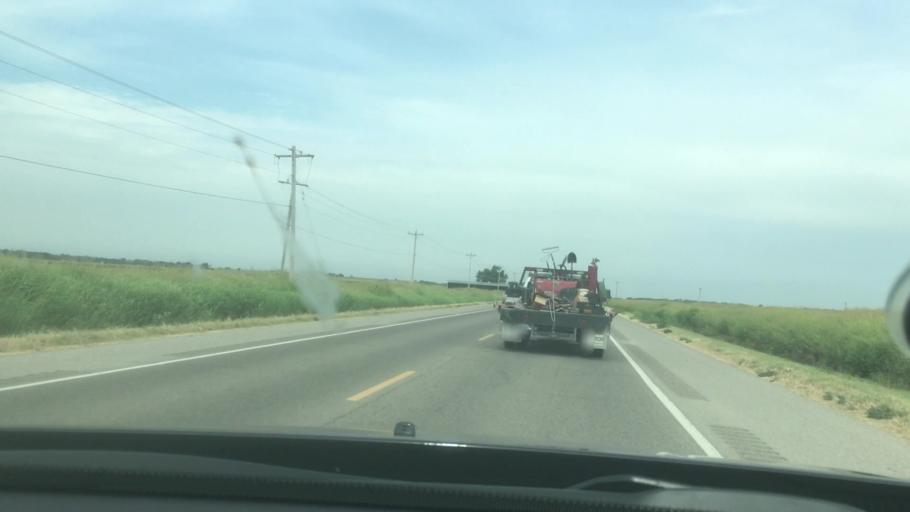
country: US
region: Oklahoma
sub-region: Garvin County
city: Lindsay
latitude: 34.8237
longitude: -97.5321
